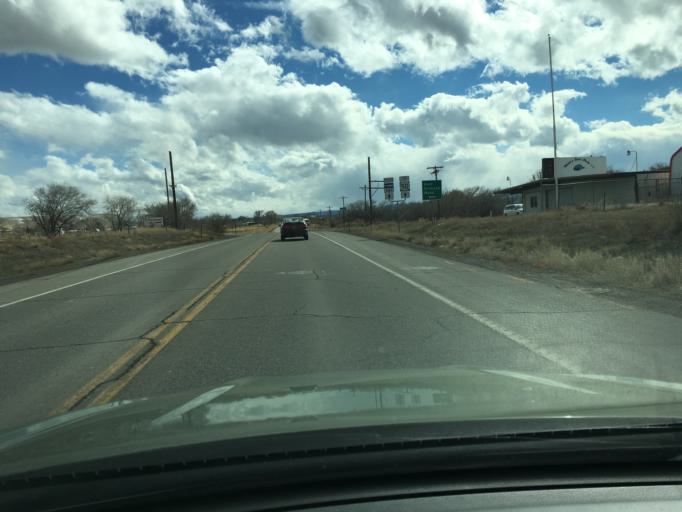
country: US
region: Colorado
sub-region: Mesa County
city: Clifton
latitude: 39.0494
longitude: -108.4596
